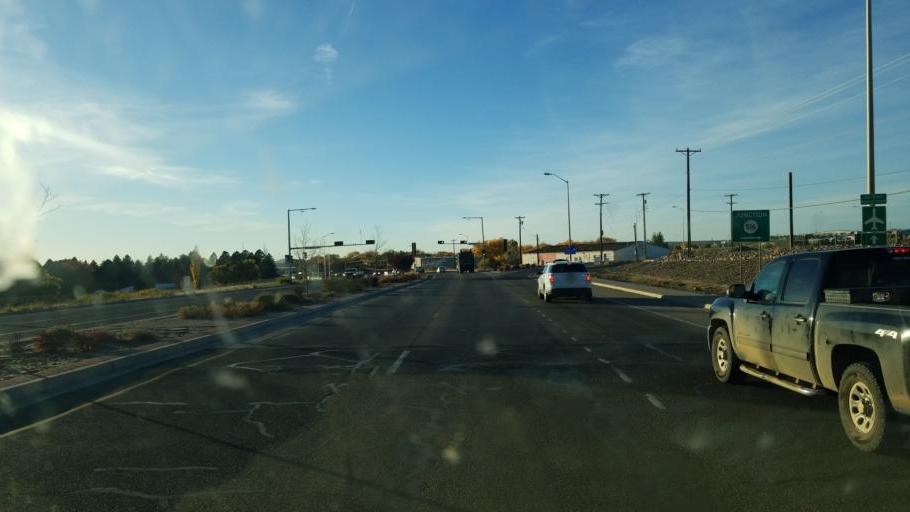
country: US
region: New Mexico
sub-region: San Juan County
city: Farmington
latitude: 36.7182
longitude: -108.1563
